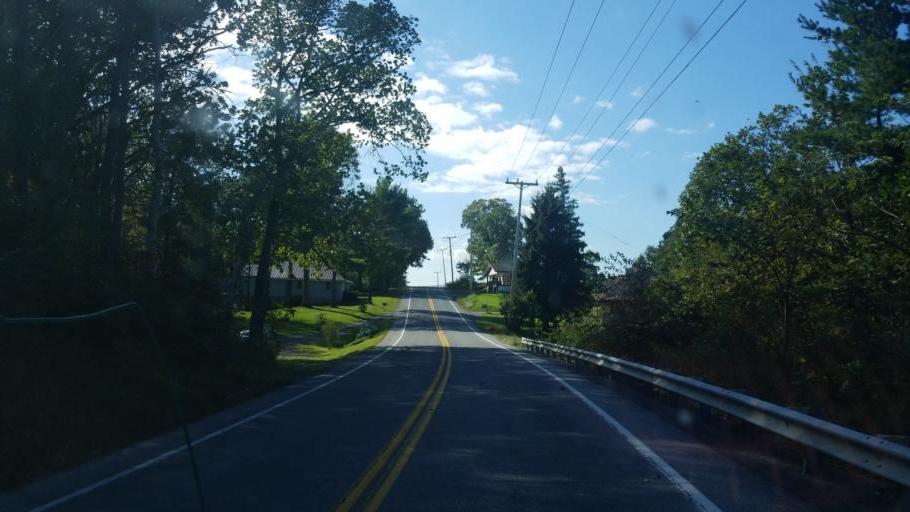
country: US
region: Pennsylvania
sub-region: Bedford County
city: Bedford
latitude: 40.1283
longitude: -78.5215
